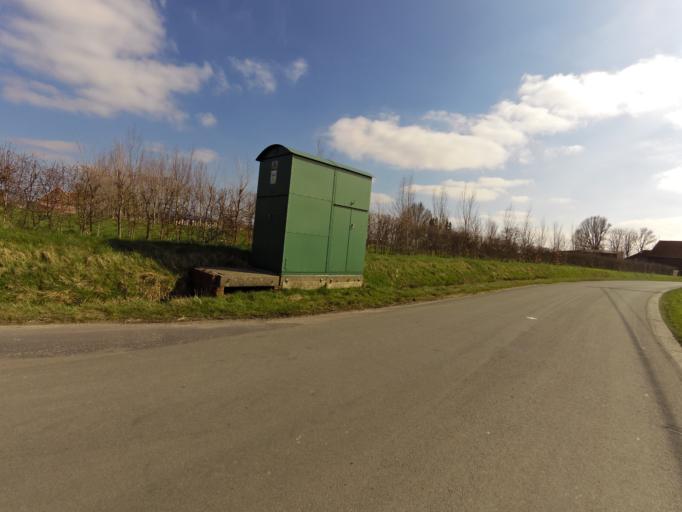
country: BE
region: Flanders
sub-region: Provincie West-Vlaanderen
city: Torhout
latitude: 51.0528
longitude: 3.0962
